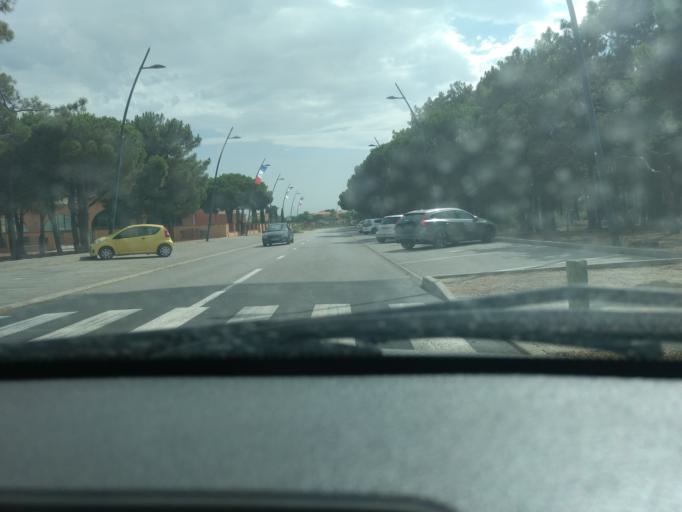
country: FR
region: Languedoc-Roussillon
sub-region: Departement des Pyrenees-Orientales
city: Le Barcares
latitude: 42.8111
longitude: 3.0346
